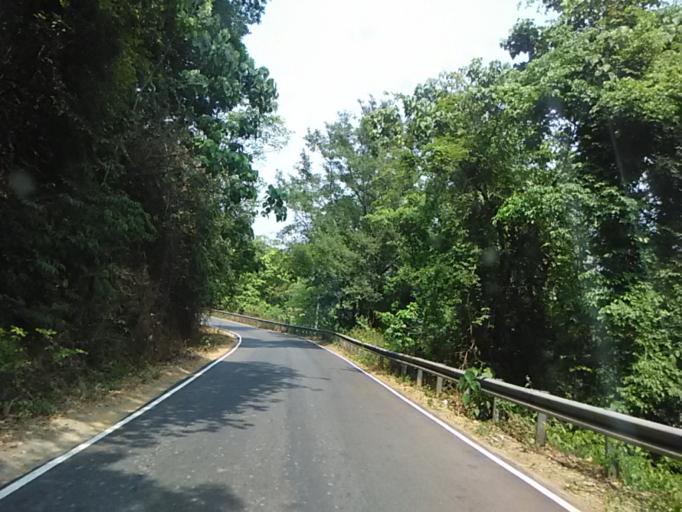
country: IN
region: Karnataka
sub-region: Kodagu
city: Virarajendrapet
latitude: 12.1164
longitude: 75.7909
